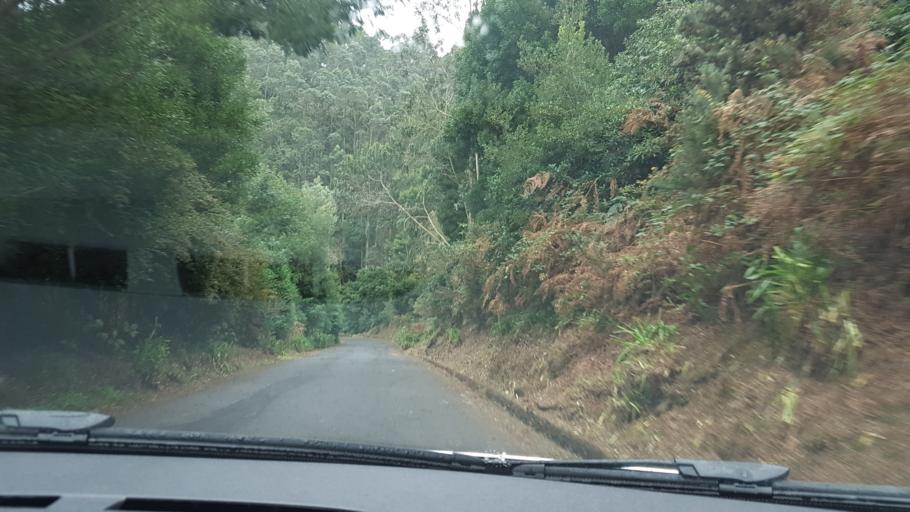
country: PT
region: Madeira
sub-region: Santa Cruz
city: Santa Cruz
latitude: 32.7277
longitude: -16.8133
